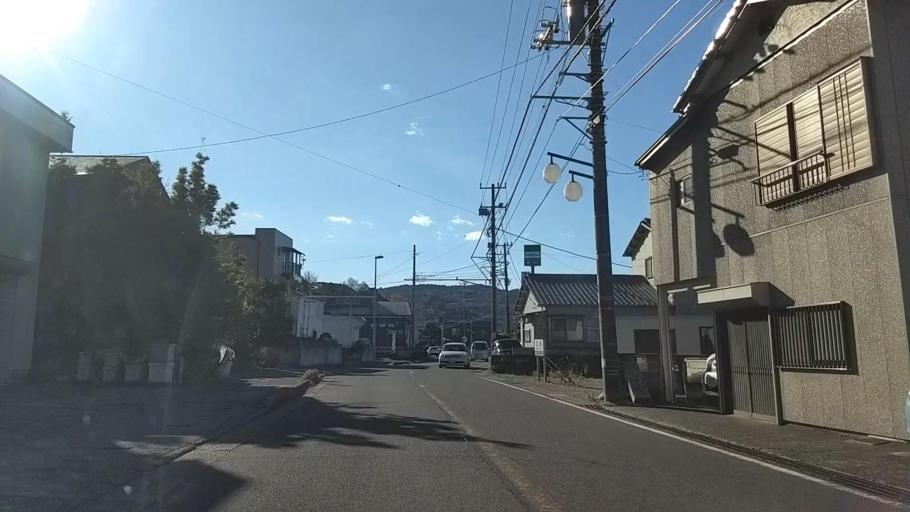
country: JP
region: Chiba
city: Futtsu
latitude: 35.2206
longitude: 139.8726
